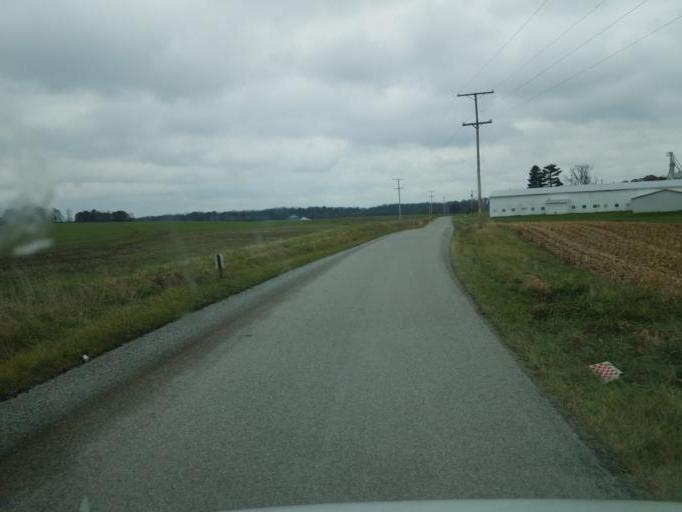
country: US
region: Ohio
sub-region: Knox County
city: Centerburg
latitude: 40.2459
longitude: -82.6412
